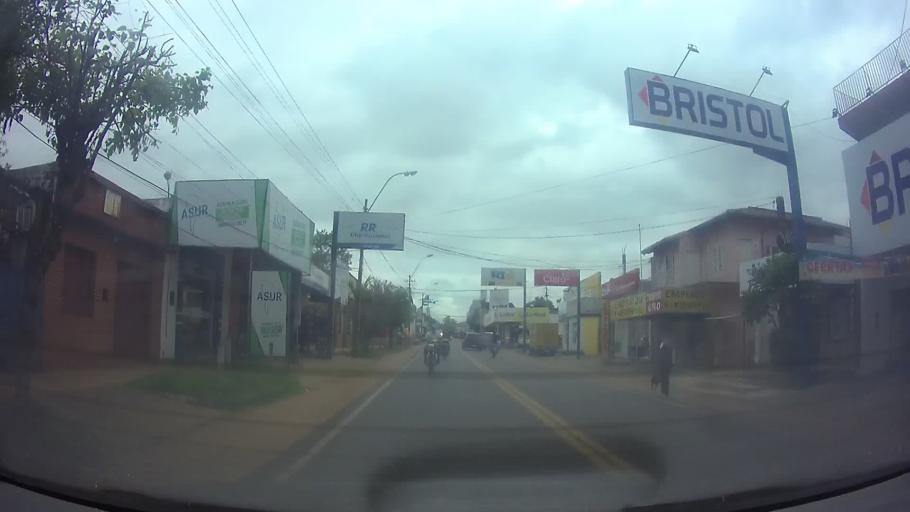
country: PY
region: Paraguari
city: Carapegua
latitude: -25.7681
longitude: -57.2408
